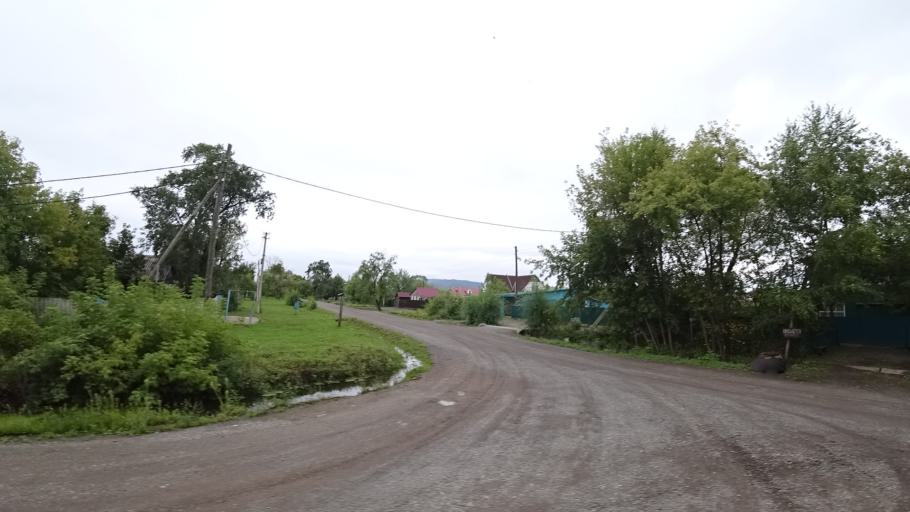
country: RU
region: Primorskiy
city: Chernigovka
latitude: 44.3450
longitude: 132.5601
